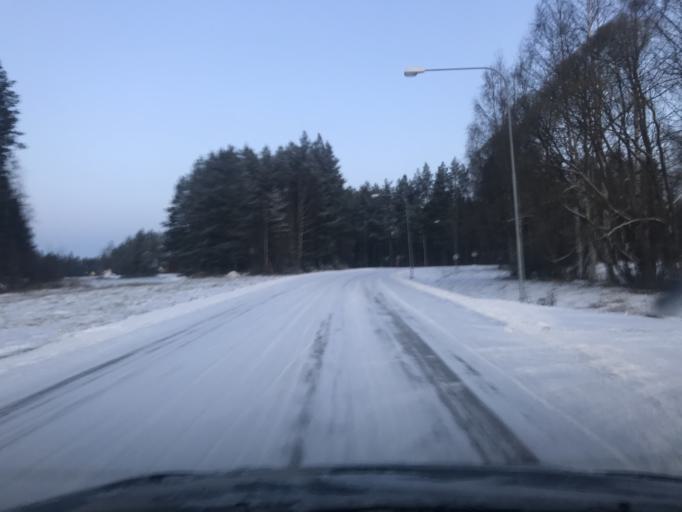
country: SE
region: Norrbotten
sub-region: Lulea Kommun
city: Bergnaset
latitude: 65.6172
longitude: 22.1221
